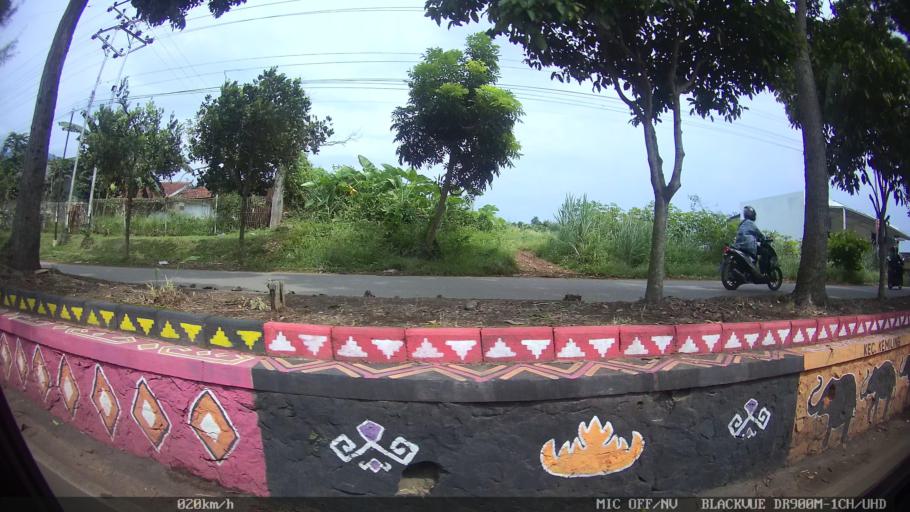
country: ID
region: Lampung
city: Bandarlampung
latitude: -5.4026
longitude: 105.2014
